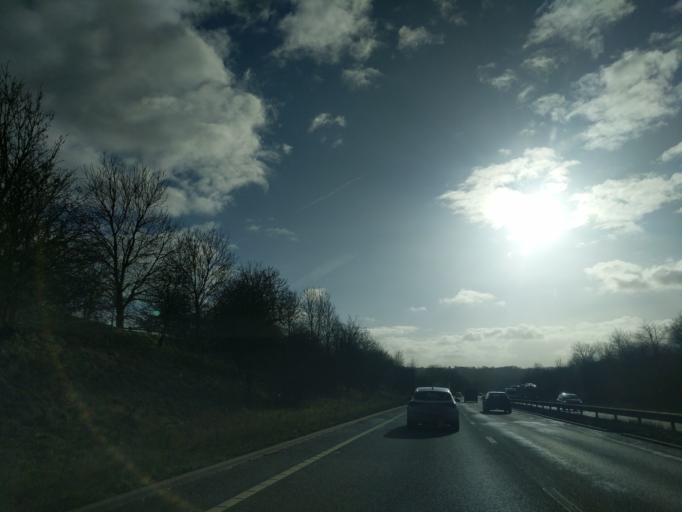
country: GB
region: England
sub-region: Derbyshire
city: Ripley
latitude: 53.0657
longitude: -1.4093
